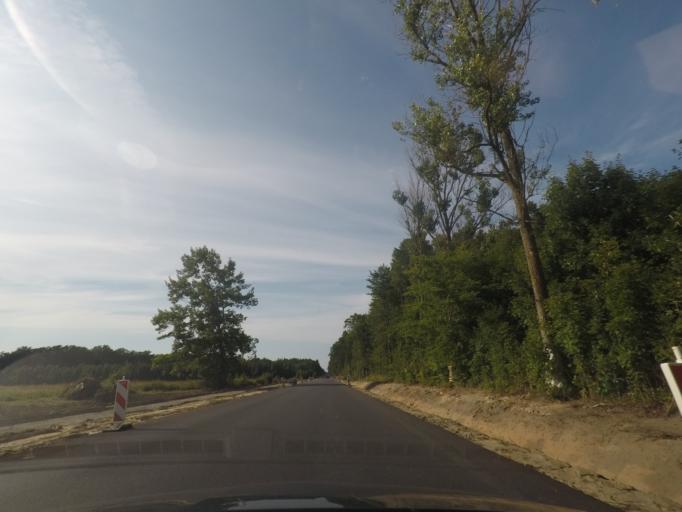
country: PL
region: Pomeranian Voivodeship
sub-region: Powiat leborski
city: Leba
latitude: 54.6931
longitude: 17.5927
